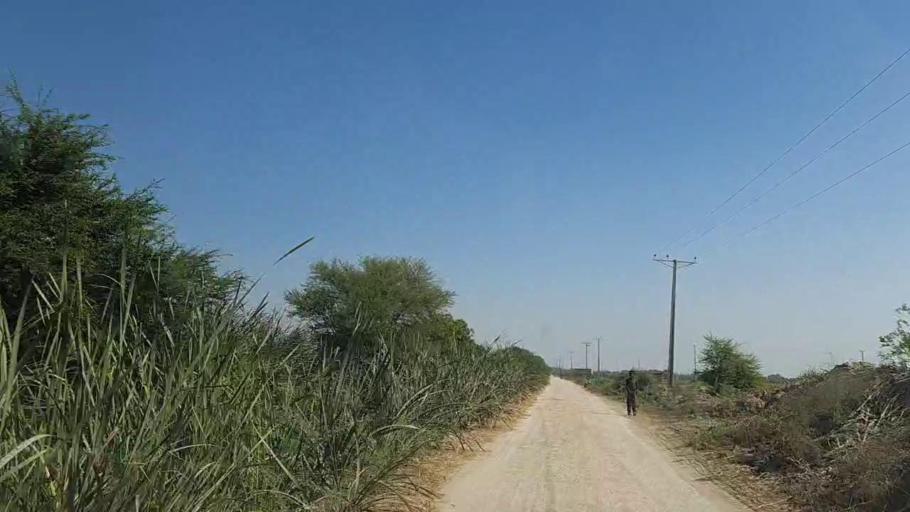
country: PK
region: Sindh
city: Daro Mehar
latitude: 24.7874
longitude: 68.1658
